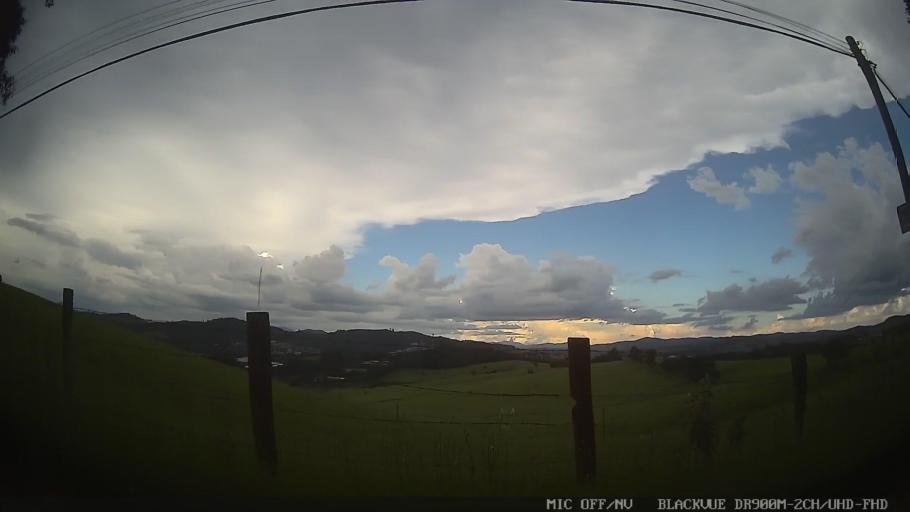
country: BR
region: Sao Paulo
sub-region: Atibaia
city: Atibaia
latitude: -23.1174
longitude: -46.5103
